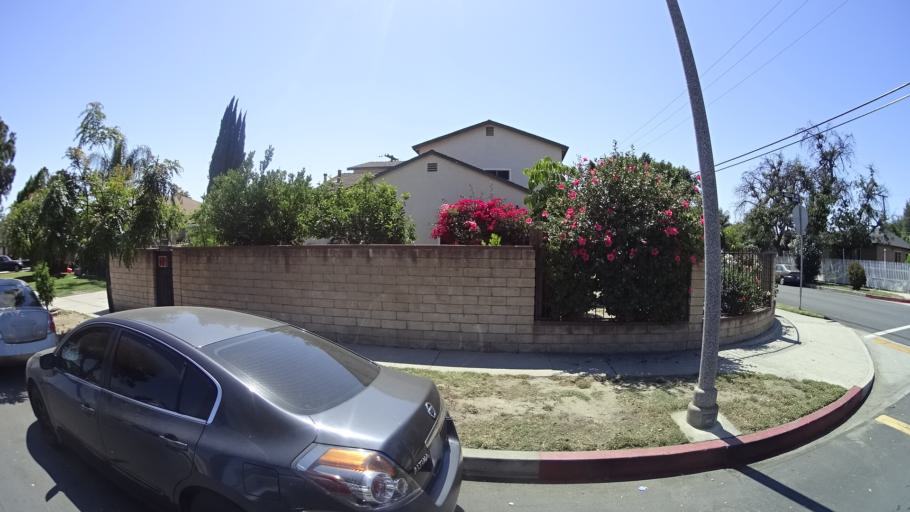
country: US
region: California
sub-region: Los Angeles County
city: Van Nuys
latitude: 34.2206
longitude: -118.4400
